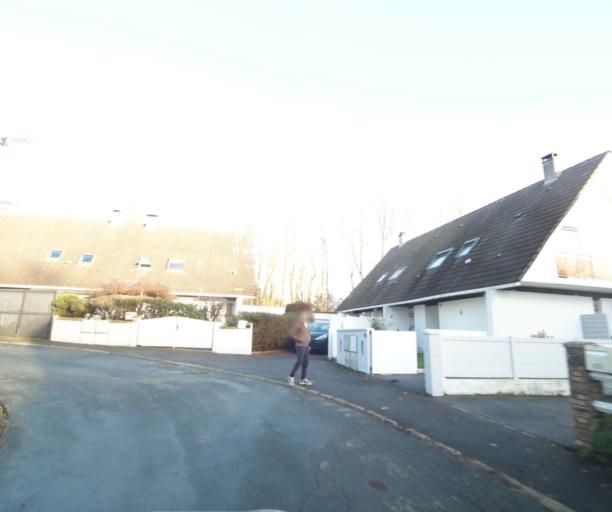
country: FR
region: Ile-de-France
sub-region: Departement des Yvelines
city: Meulan-en-Yvelines
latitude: 49.0120
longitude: 1.9307
